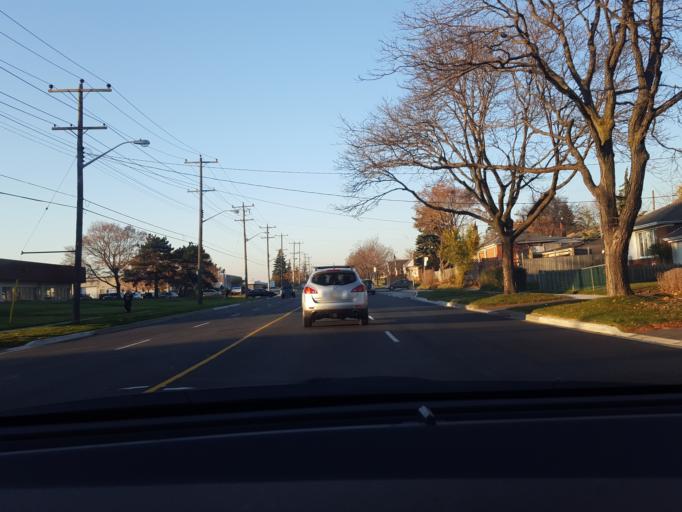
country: CA
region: Ontario
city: Scarborough
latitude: 43.7510
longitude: -79.2863
